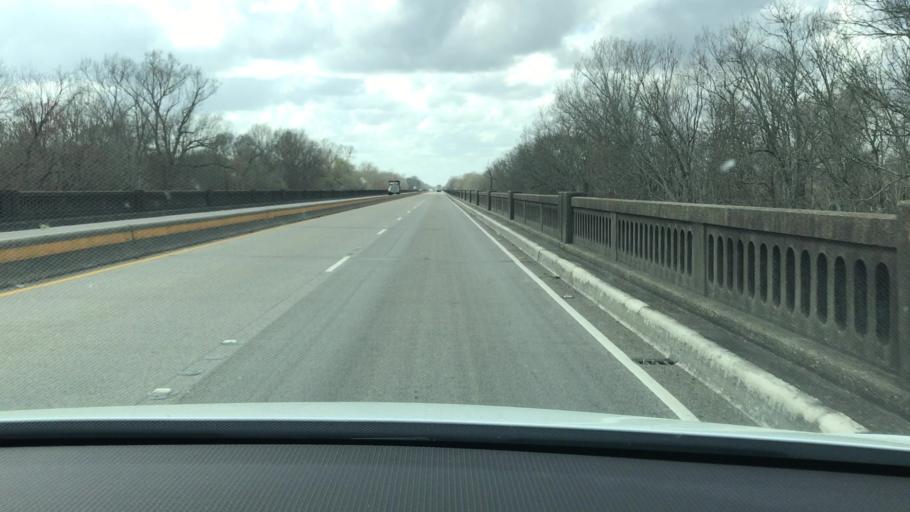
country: US
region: Louisiana
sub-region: Saint Landry Parish
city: Krotz Springs
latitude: 30.5549
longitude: -91.6860
